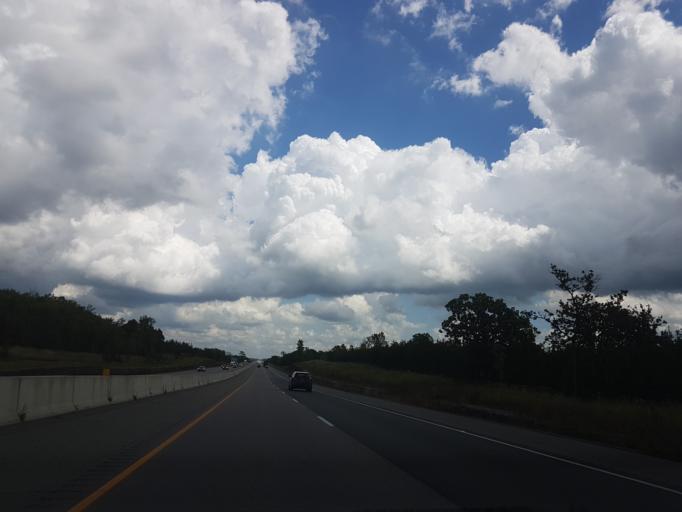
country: CA
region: Ontario
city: Deseronto
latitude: 44.2231
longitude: -77.2177
